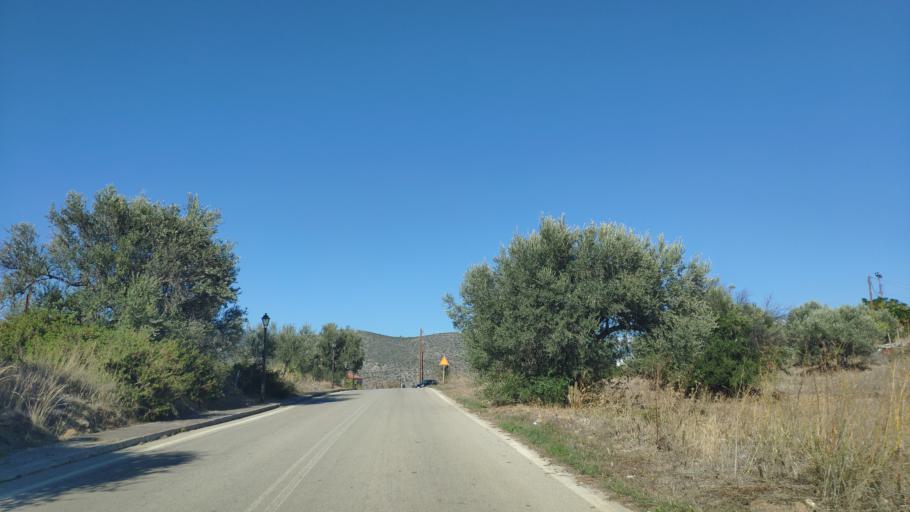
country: GR
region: Attica
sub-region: Nomos Piraios
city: Galatas
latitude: 37.5449
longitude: 23.3713
